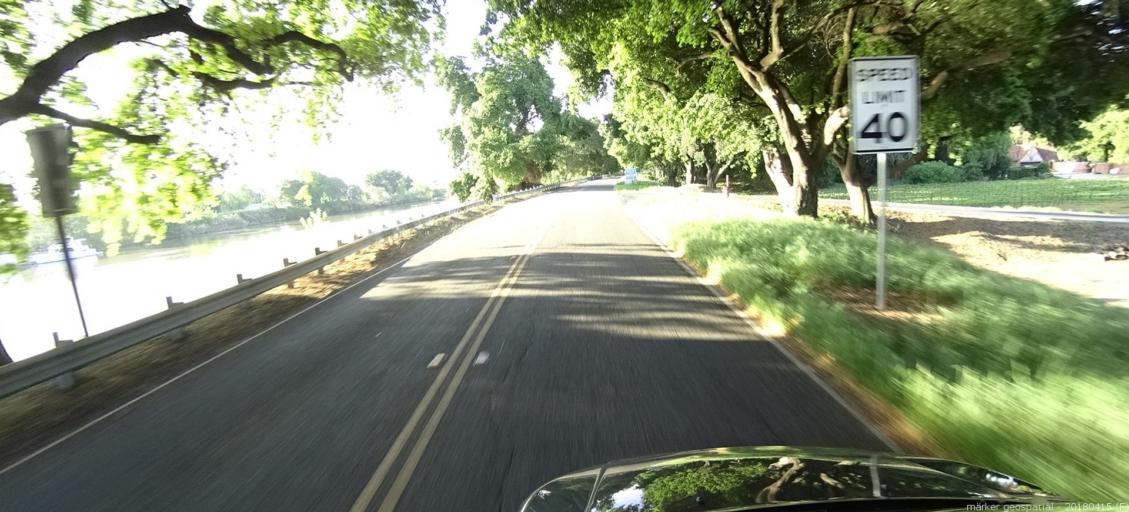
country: US
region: California
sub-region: Sacramento County
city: Walnut Grove
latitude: 38.2500
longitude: -121.5118
